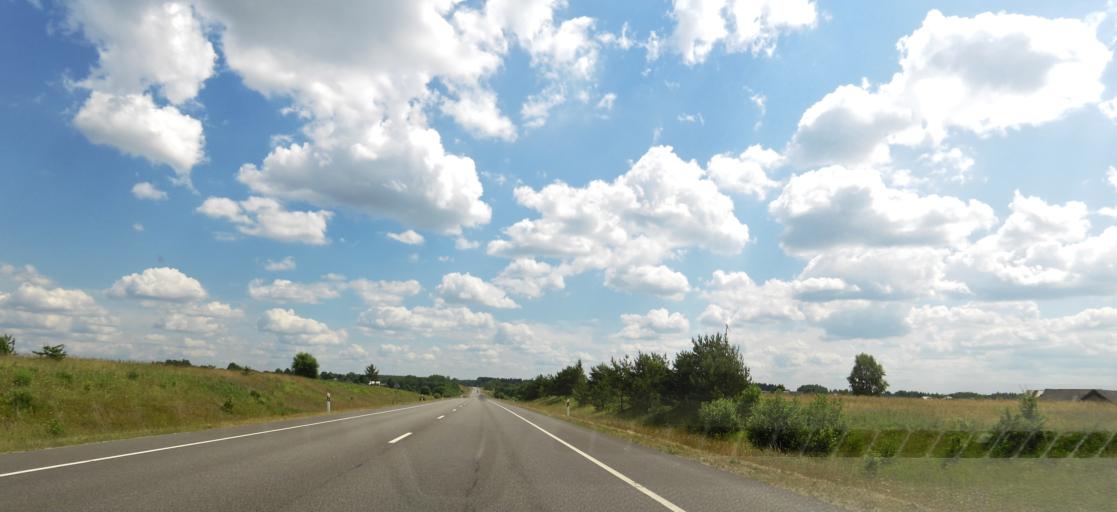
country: LT
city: Skaidiskes
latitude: 54.6222
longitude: 25.4036
